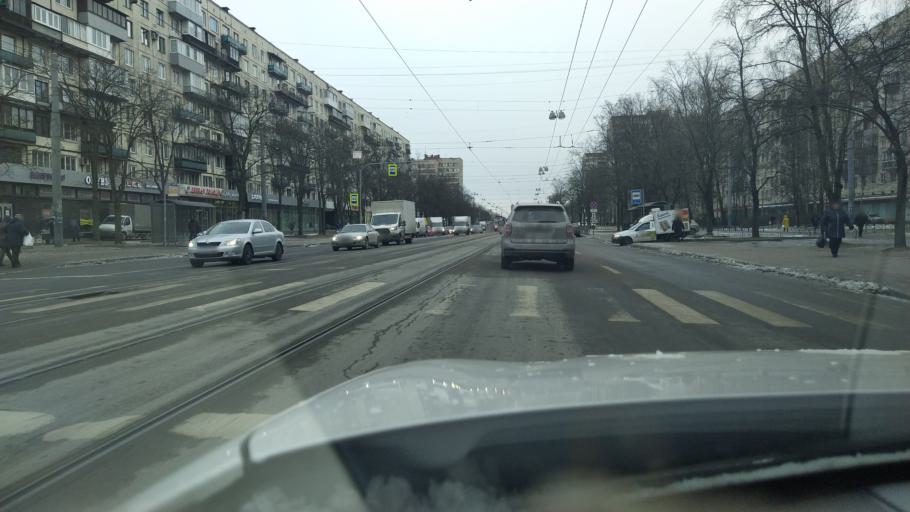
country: RU
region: Leningrad
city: Akademicheskoe
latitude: 60.0085
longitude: 30.4158
